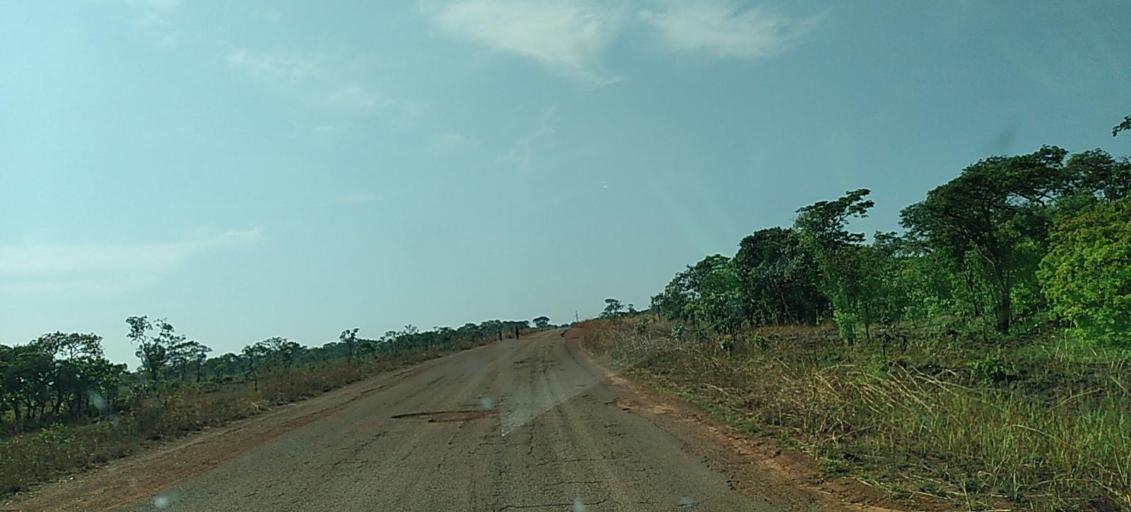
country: ZM
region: North-Western
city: Mwinilunga
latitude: -11.7783
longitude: 25.0212
